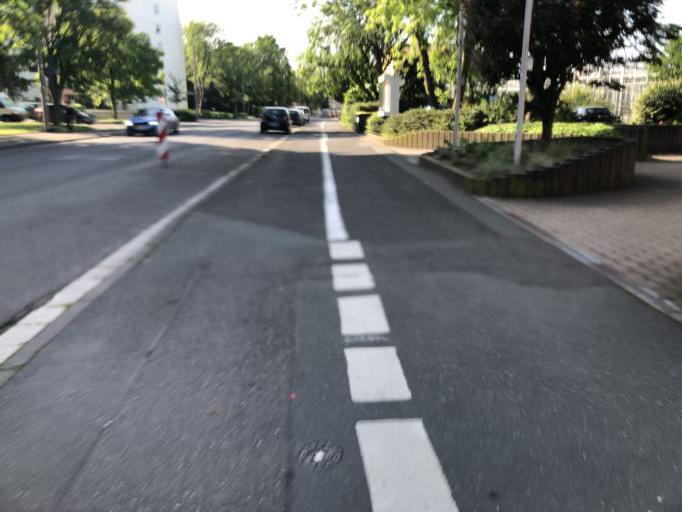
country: DE
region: Bavaria
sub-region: Regierungsbezirk Mittelfranken
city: Erlangen
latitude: 49.5778
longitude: 10.9922
